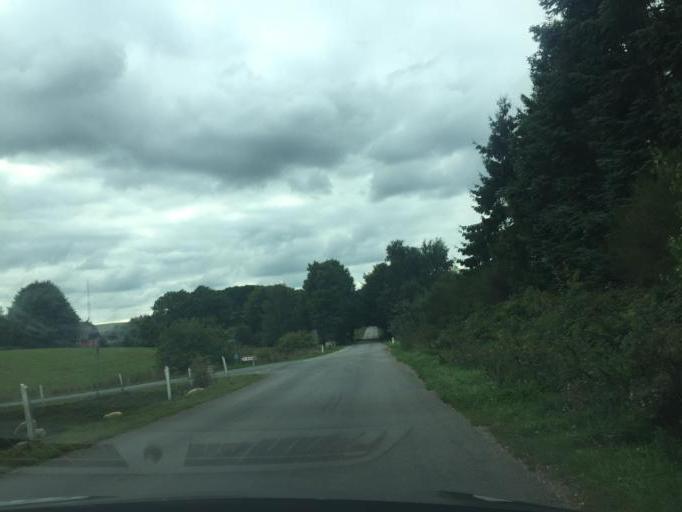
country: DK
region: South Denmark
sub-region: Assens Kommune
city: Tommerup Stationsby
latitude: 55.3566
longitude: 10.2086
